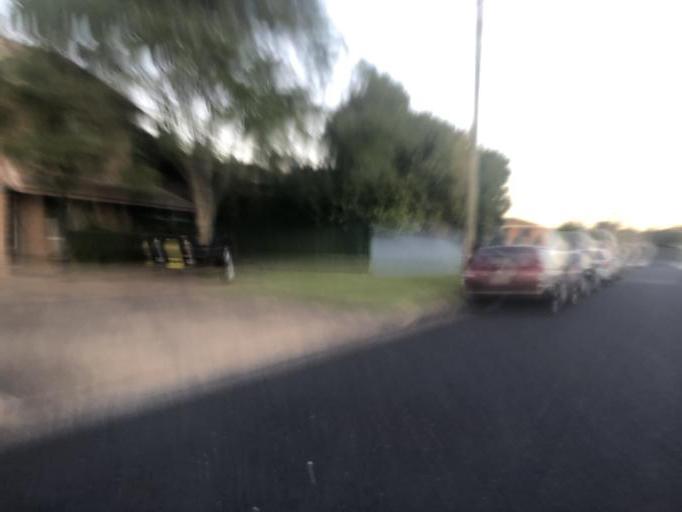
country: AU
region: New South Wales
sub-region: Coffs Harbour
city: Coffs Harbour
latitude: -30.2873
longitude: 153.1339
